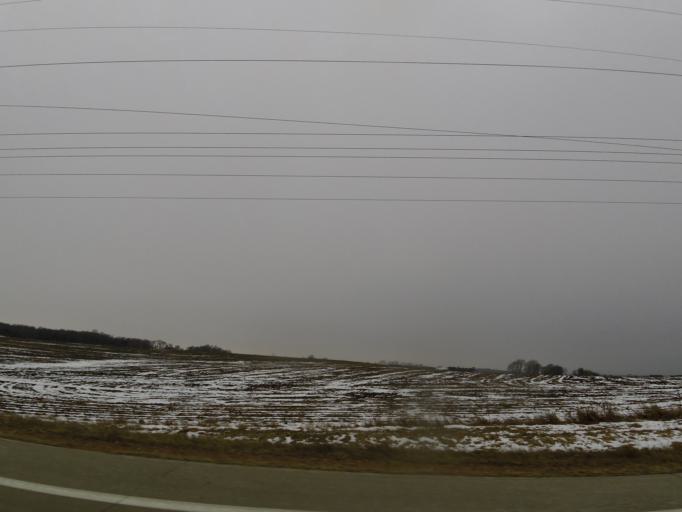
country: US
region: Minnesota
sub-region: Scott County
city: Jordan
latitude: 44.6472
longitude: -93.6266
